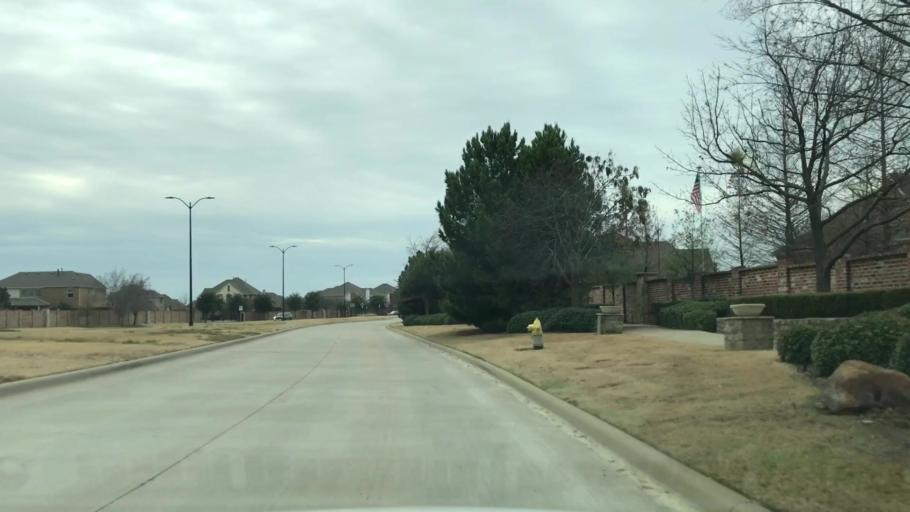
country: US
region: Texas
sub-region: Denton County
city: The Colony
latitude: 33.1256
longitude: -96.8960
